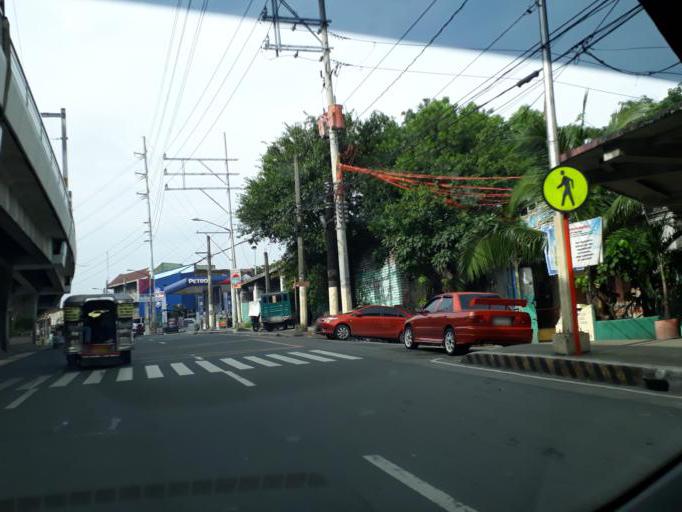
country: PH
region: Metro Manila
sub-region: City of Manila
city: Manila
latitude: 14.6373
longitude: 120.9829
